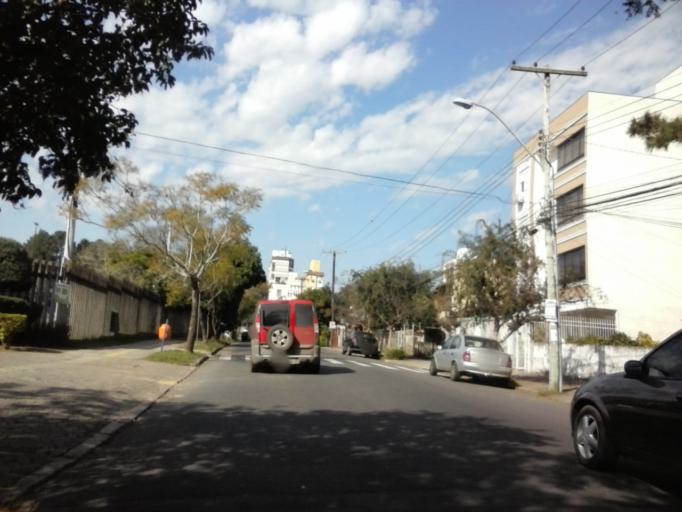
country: BR
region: Rio Grande do Sul
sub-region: Porto Alegre
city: Porto Alegre
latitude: -30.0514
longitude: -51.1827
